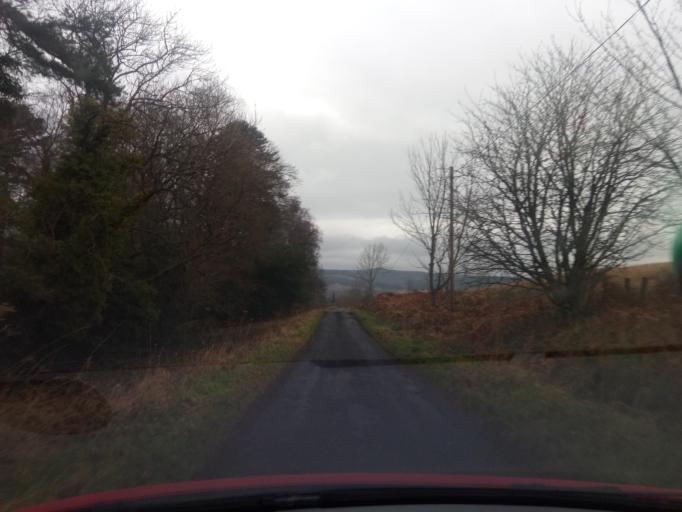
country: GB
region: England
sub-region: Northumberland
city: Rochester
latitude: 55.1755
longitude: -2.4267
